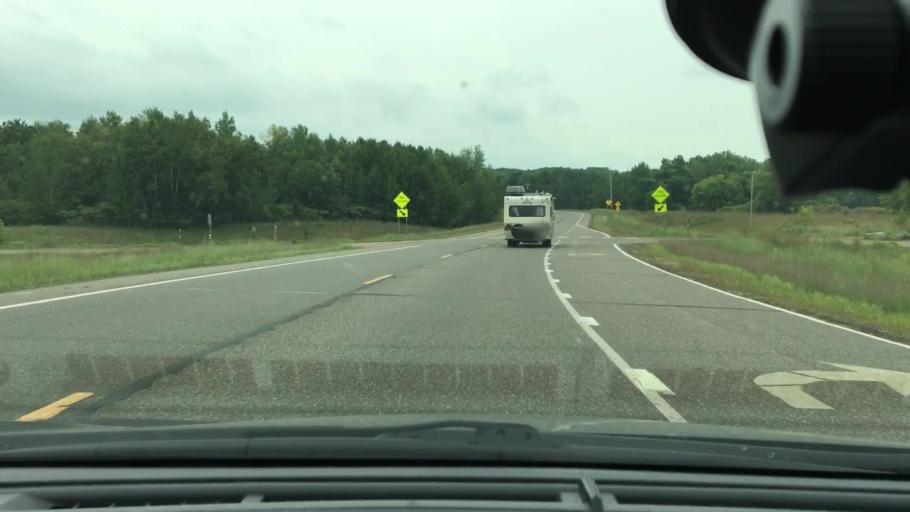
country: US
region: Minnesota
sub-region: Crow Wing County
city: Crosby
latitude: 46.4917
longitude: -93.9560
